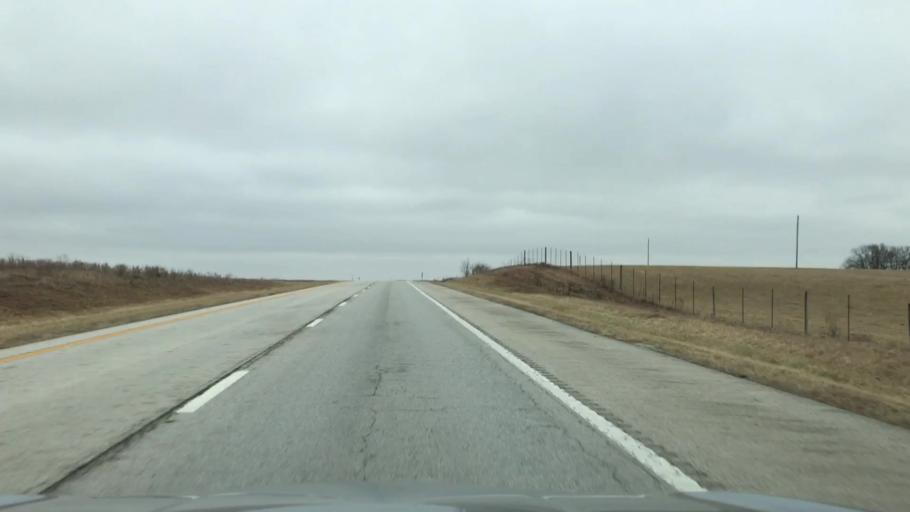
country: US
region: Missouri
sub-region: Linn County
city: Marceline
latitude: 39.7593
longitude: -92.8878
